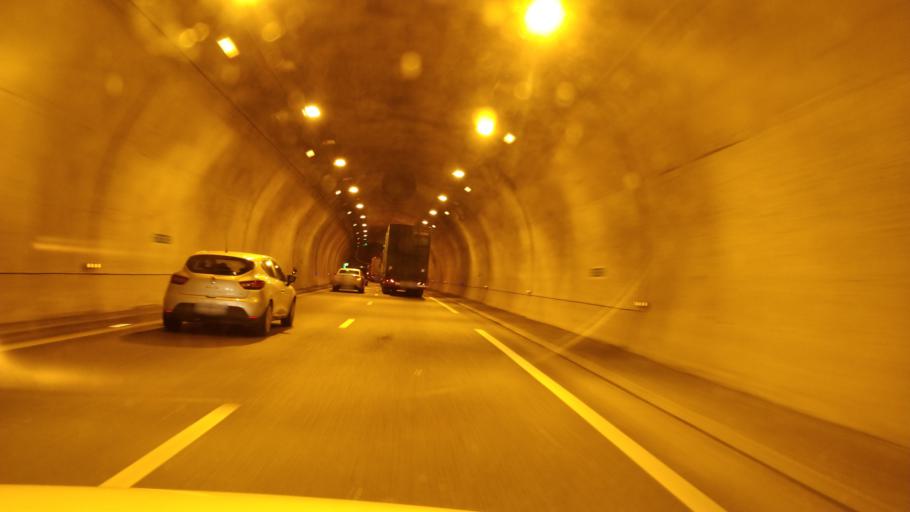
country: FR
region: Haute-Normandie
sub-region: Departement de la Seine-Maritime
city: Bihorel
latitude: 49.4407
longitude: 1.1330
